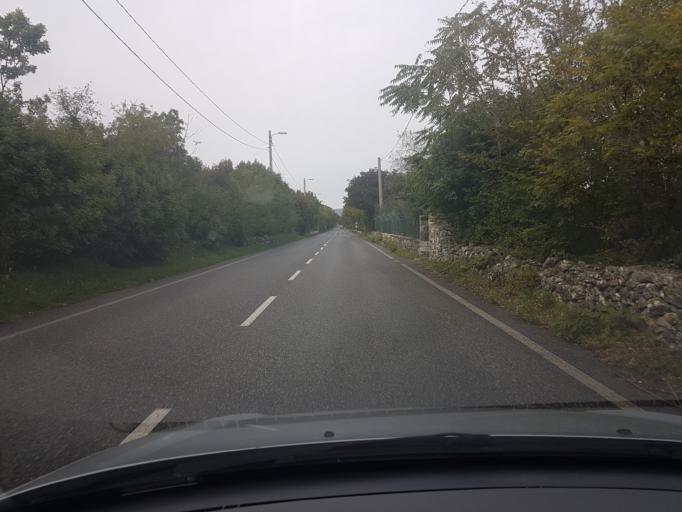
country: IT
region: Friuli Venezia Giulia
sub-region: Provincia di Trieste
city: Santa Croce
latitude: 45.7406
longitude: 13.6855
